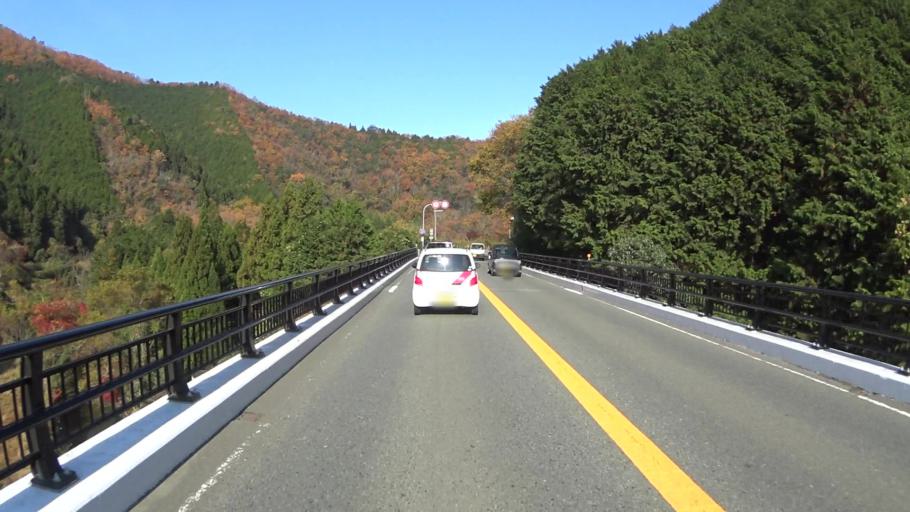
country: JP
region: Kyoto
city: Ayabe
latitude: 35.2008
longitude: 135.2817
